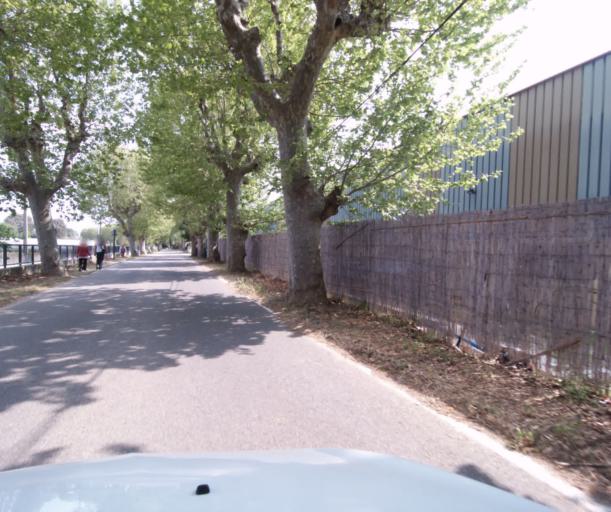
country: FR
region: Provence-Alpes-Cote d'Azur
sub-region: Departement du Var
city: Hyeres
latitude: 43.1054
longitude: 6.1442
